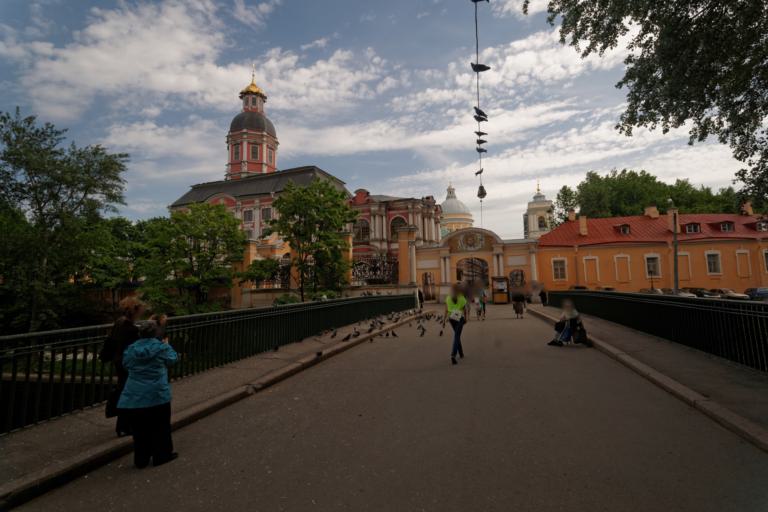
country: RU
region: St.-Petersburg
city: Centralniy
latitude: 59.9225
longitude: 30.3874
